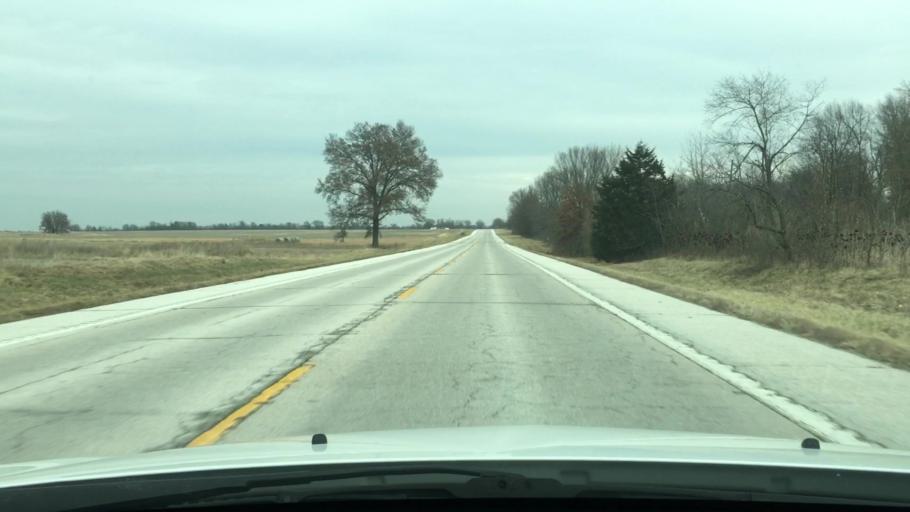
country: US
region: Missouri
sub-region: Audrain County
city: Vandalia
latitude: 39.3264
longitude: -91.4480
